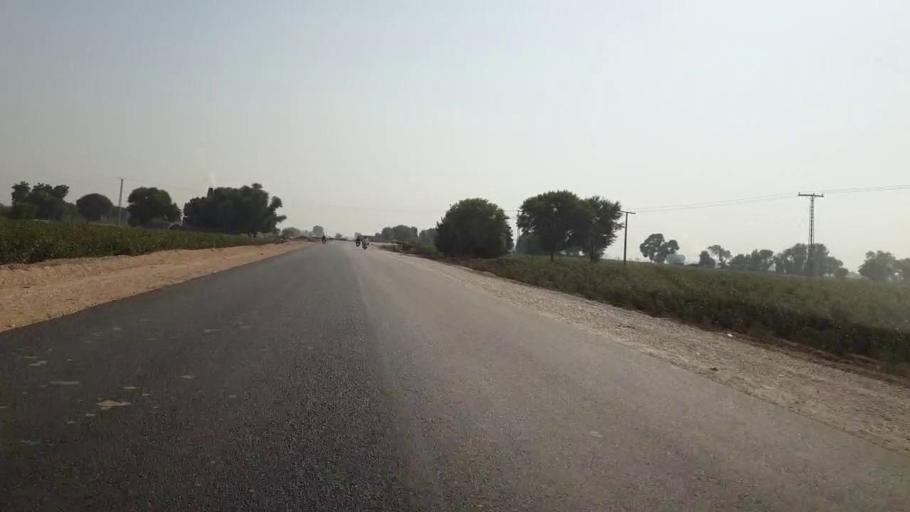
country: PK
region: Sindh
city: Dadu
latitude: 26.6786
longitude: 67.7764
